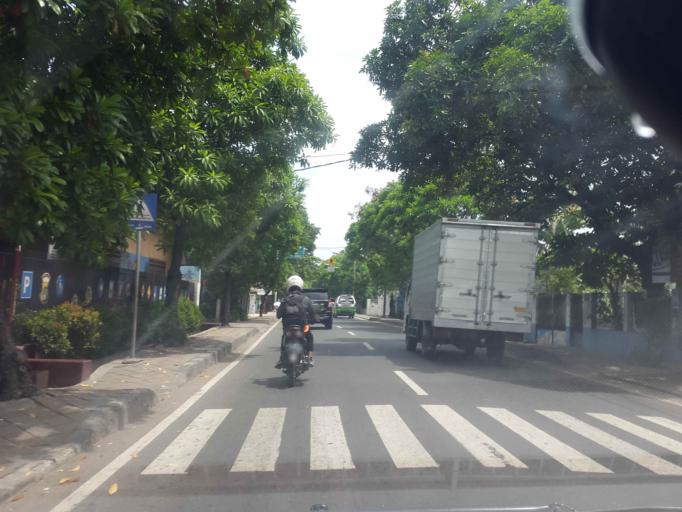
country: ID
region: Banten
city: Tangerang
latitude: -6.1679
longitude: 106.6293
